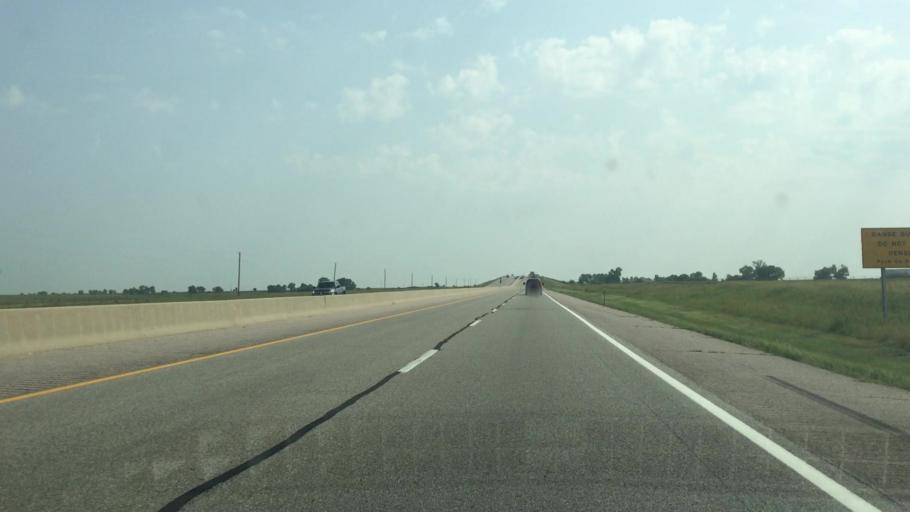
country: US
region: Kansas
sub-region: Chase County
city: Cottonwood Falls
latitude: 38.0579
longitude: -96.6235
